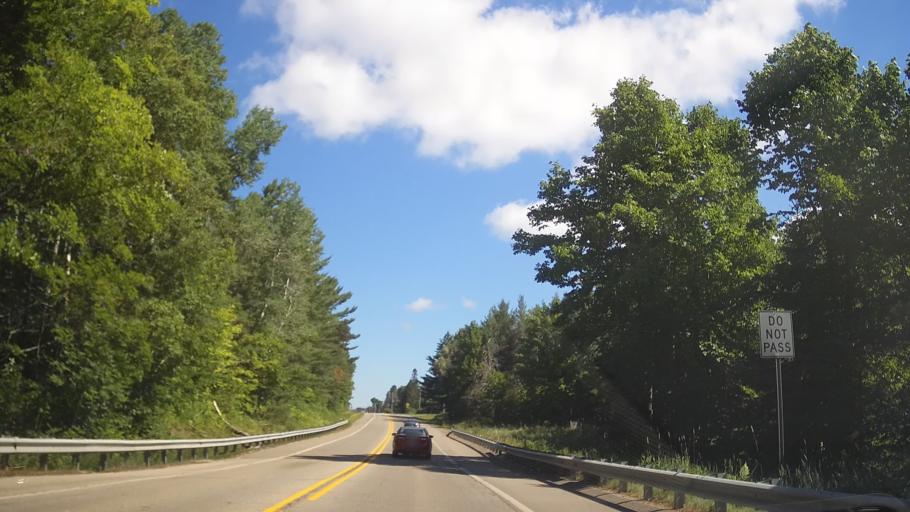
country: US
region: Michigan
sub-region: Cheboygan County
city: Indian River
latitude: 45.4684
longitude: -84.7812
